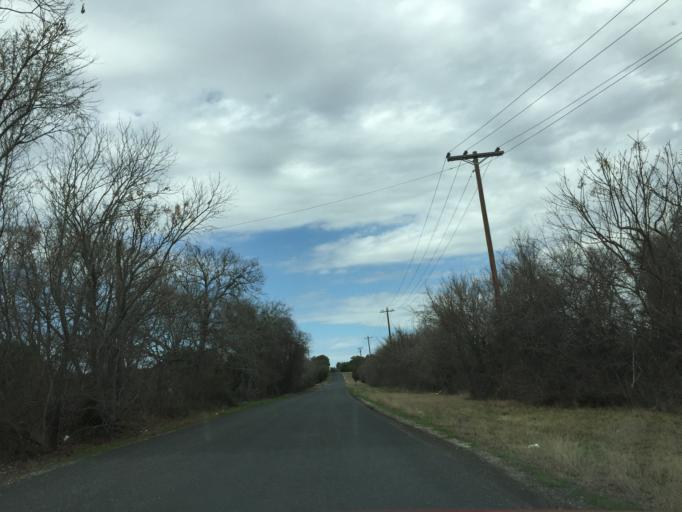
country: US
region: Texas
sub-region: Burnet County
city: Bertram
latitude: 30.7381
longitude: -97.9367
